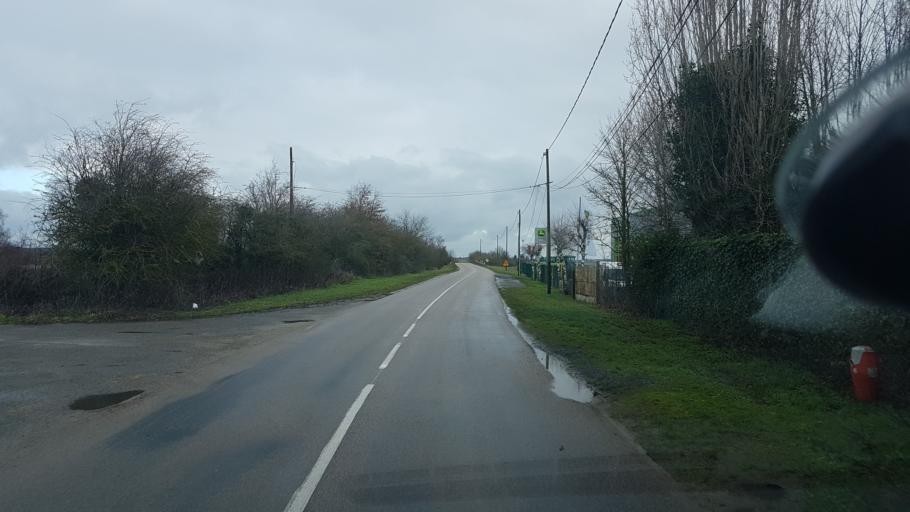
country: FR
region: Ile-de-France
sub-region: Departement de Seine-et-Marne
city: Souppes-sur-Loing
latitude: 48.2081
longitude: 2.7850
